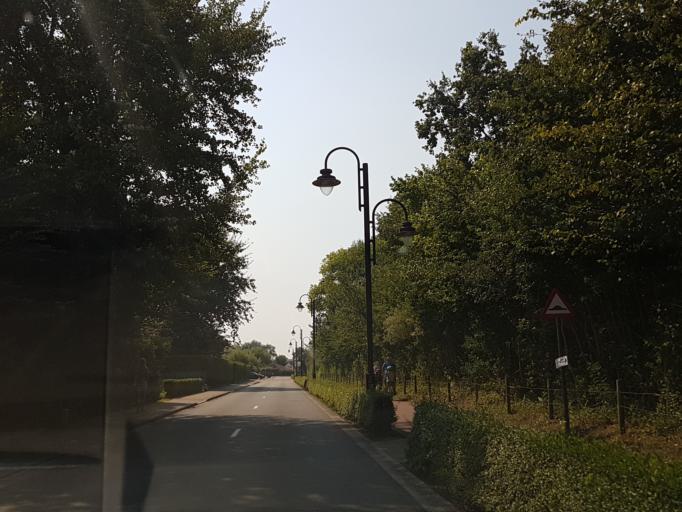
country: BE
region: Flanders
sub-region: Provincie West-Vlaanderen
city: De Haan
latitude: 51.2692
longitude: 3.0253
